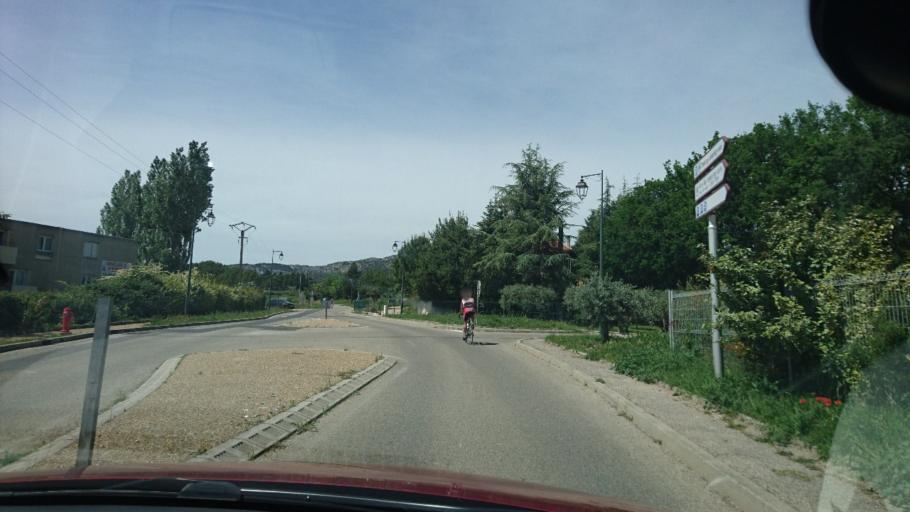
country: FR
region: Provence-Alpes-Cote d'Azur
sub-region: Departement du Vaucluse
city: Bedoin
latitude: 44.1283
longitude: 5.1776
